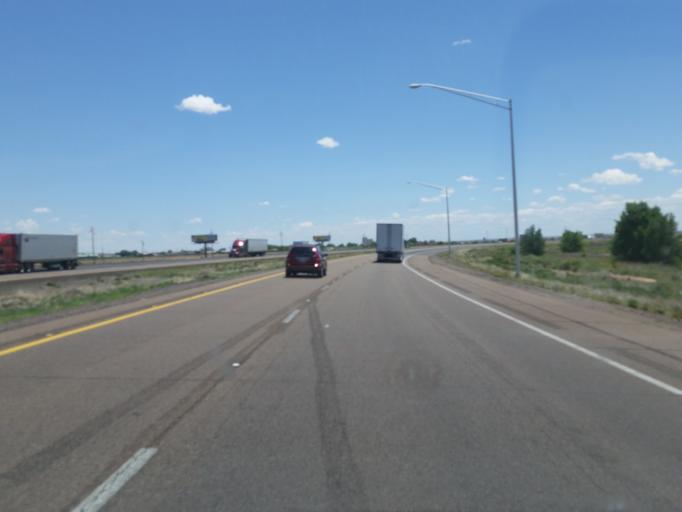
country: US
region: Arizona
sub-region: Navajo County
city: Winslow
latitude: 35.0372
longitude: -110.6901
